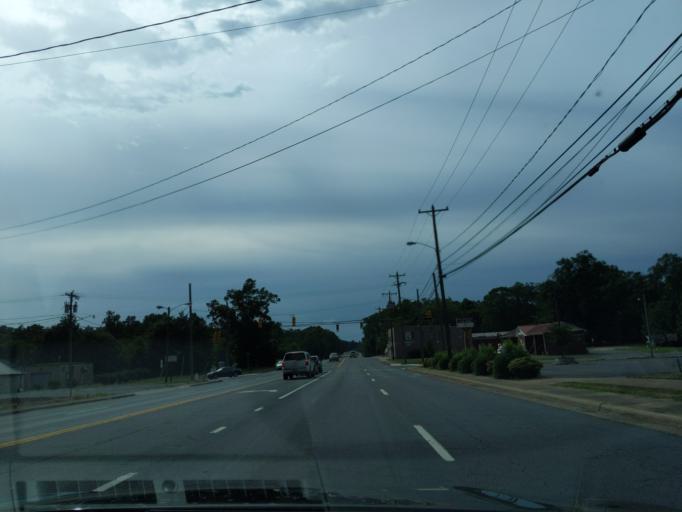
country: US
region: North Carolina
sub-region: Stanly County
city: Albemarle
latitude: 35.4675
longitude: -80.2589
